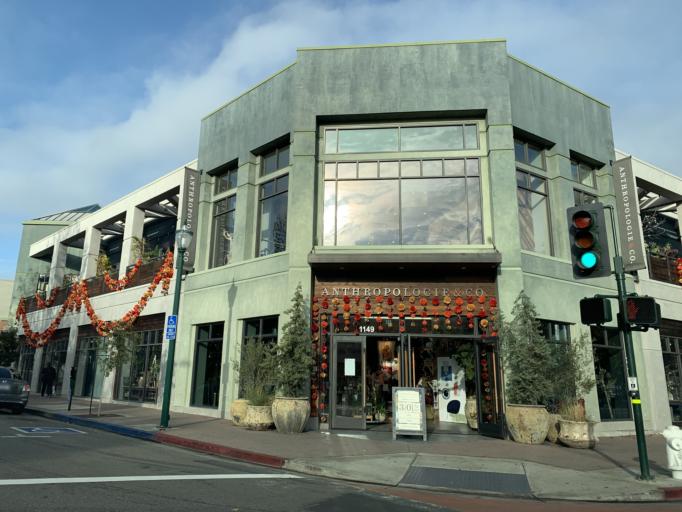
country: US
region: California
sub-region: Contra Costa County
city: Walnut Creek
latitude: 37.8963
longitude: -122.0600
